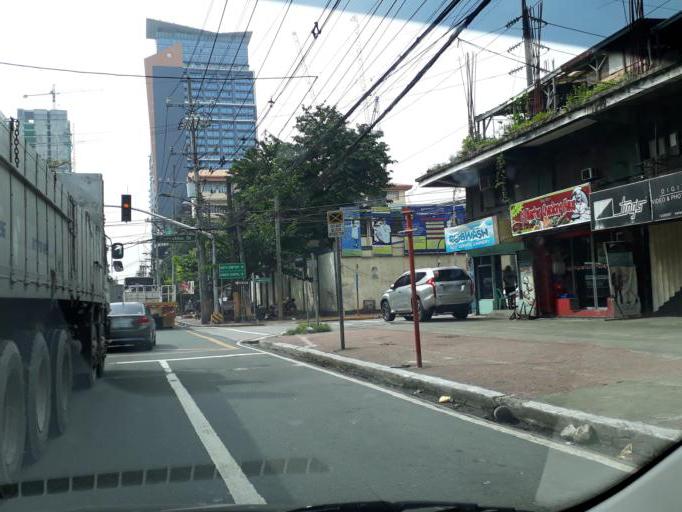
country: PH
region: Metro Manila
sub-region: City of Manila
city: Manila
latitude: 14.6106
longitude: 120.9918
